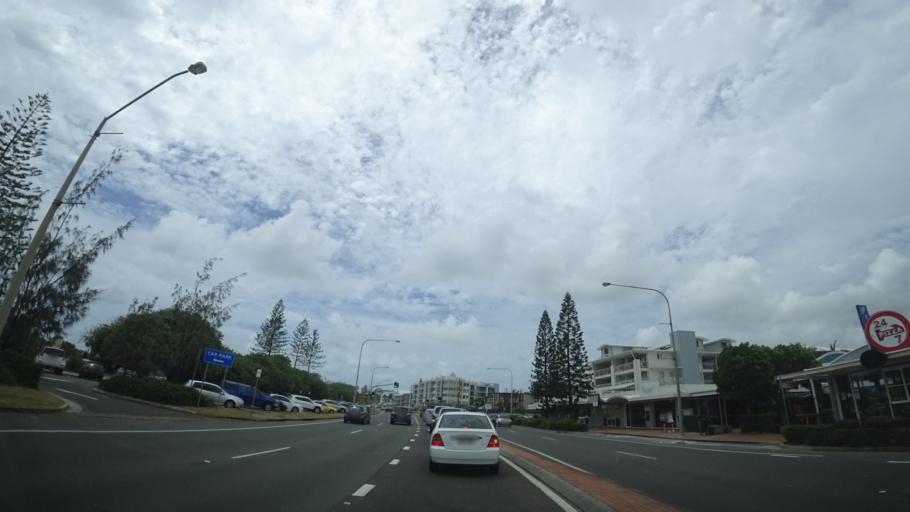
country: AU
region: Queensland
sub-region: Sunshine Coast
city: Mooloolaba
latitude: -26.6698
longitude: 153.1074
